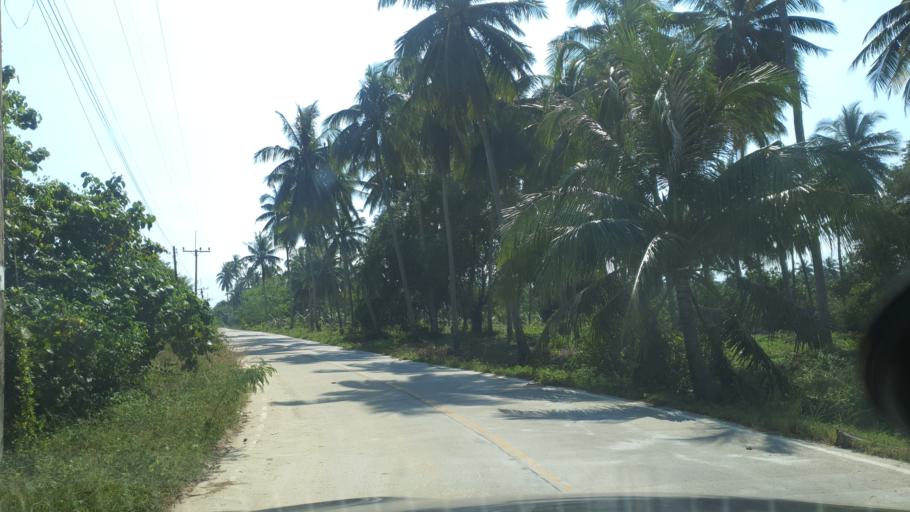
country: TH
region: Surat Thani
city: Tha Chana
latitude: 9.6009
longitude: 99.2062
